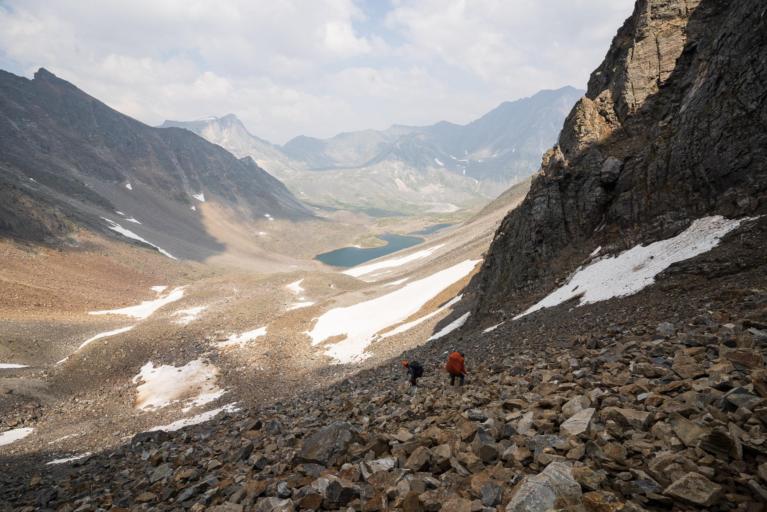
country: RU
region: Transbaikal Territory
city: Chara
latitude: 56.8100
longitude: 117.1209
